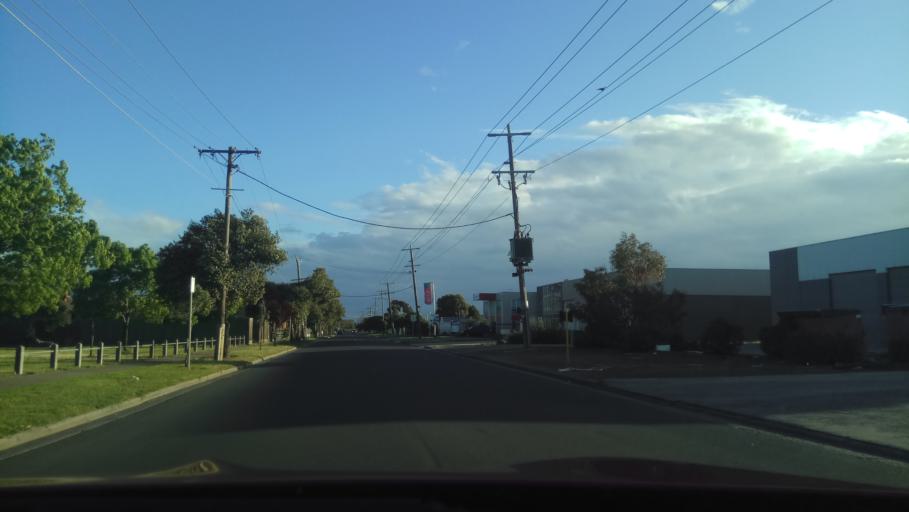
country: AU
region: Victoria
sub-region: Hobsons Bay
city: Altona North
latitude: -37.8392
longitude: 144.8419
